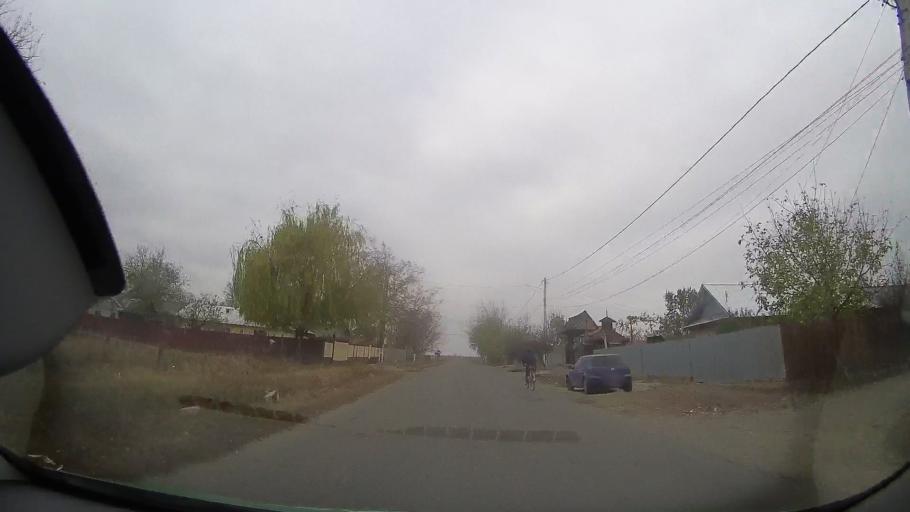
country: RO
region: Buzau
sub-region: Comuna Luciu
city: Luciu
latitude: 44.9744
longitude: 27.0685
